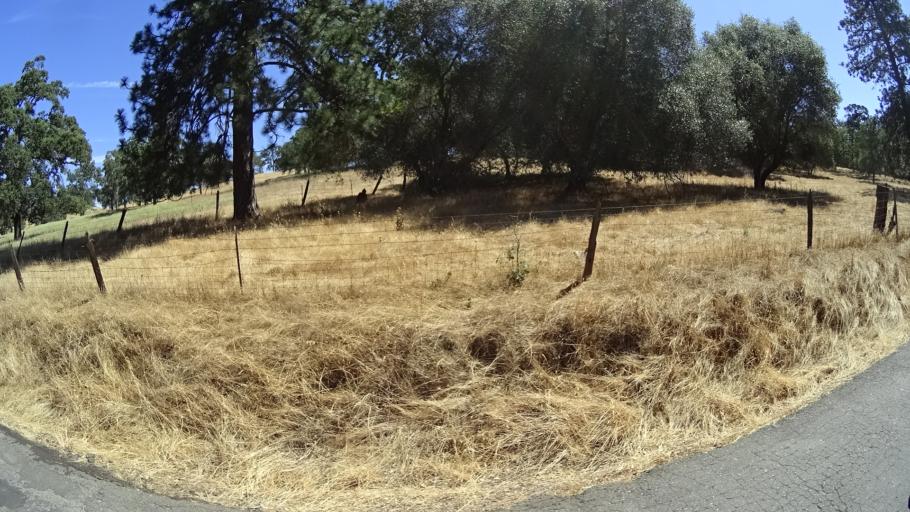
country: US
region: California
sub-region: Calaveras County
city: Angels Camp
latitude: 38.1051
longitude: -120.5670
